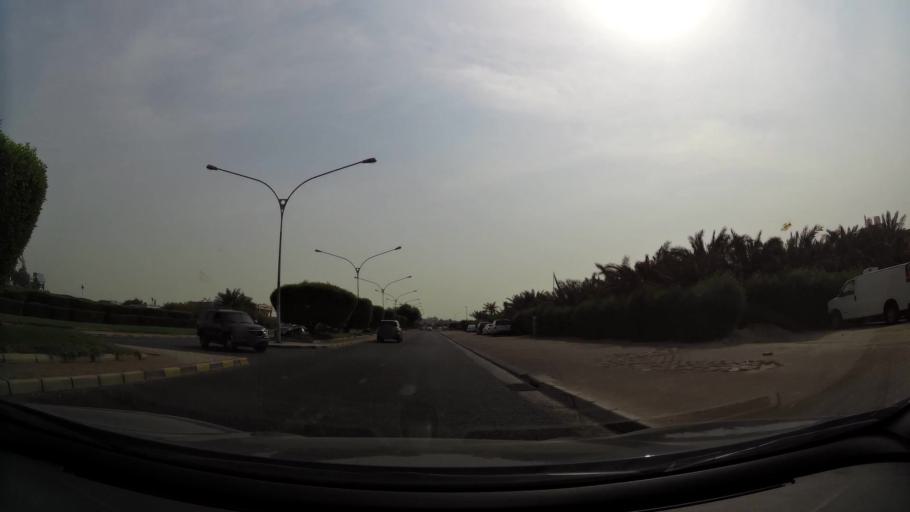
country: KW
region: Al Asimah
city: Ar Rabiyah
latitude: 29.2920
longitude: 47.9393
